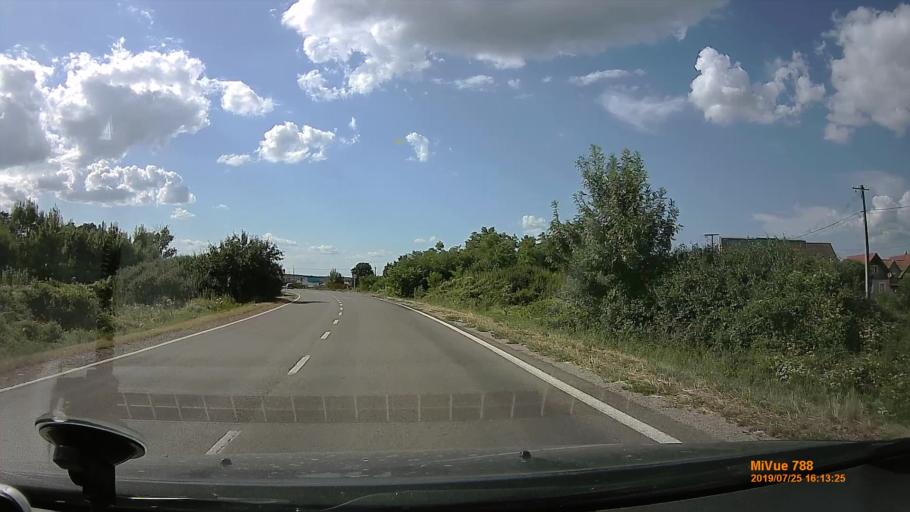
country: HU
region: Heves
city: Kerecsend
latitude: 47.7923
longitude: 20.3403
